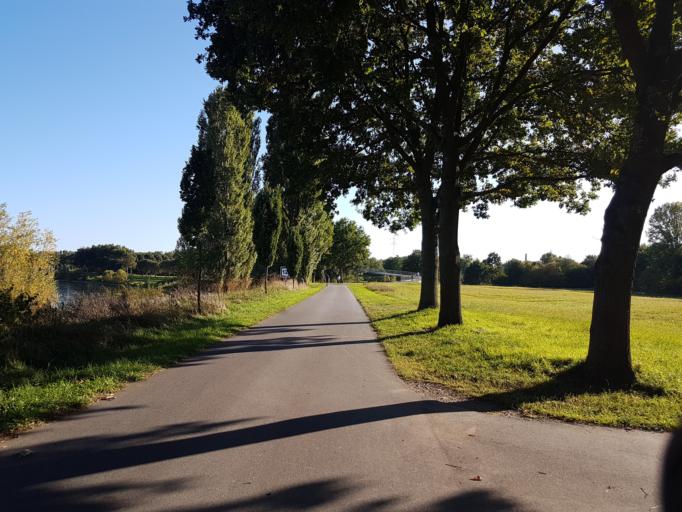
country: DE
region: North Rhine-Westphalia
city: Bad Oeynhausen
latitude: 52.2224
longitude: 8.8275
